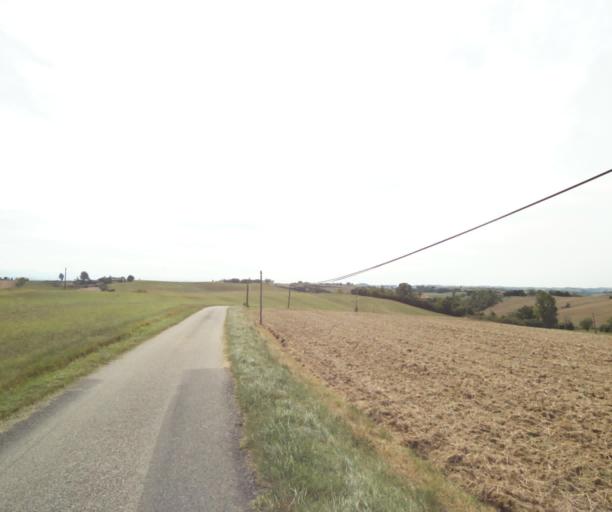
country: FR
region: Midi-Pyrenees
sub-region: Departement de la Haute-Garonne
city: Gaillac-Toulza
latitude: 43.2450
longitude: 1.4149
